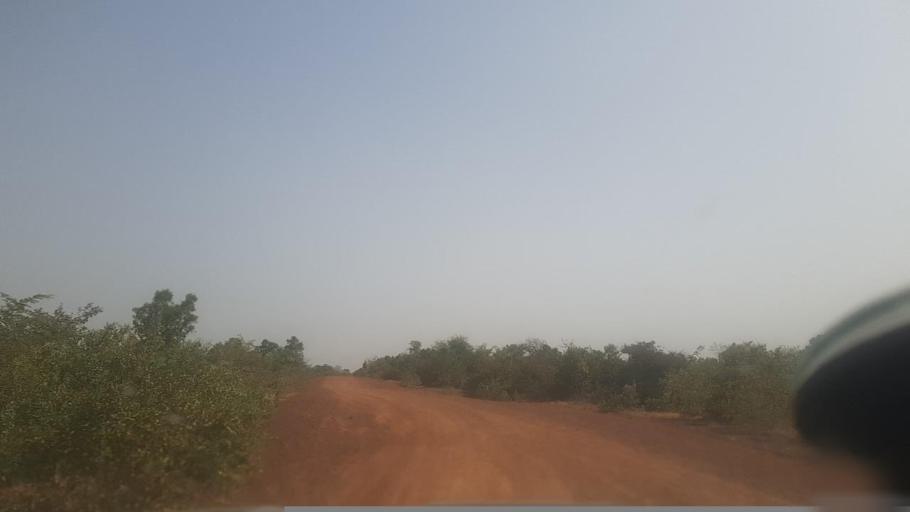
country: ML
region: Segou
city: Segou
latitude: 12.9292
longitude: -6.2784
